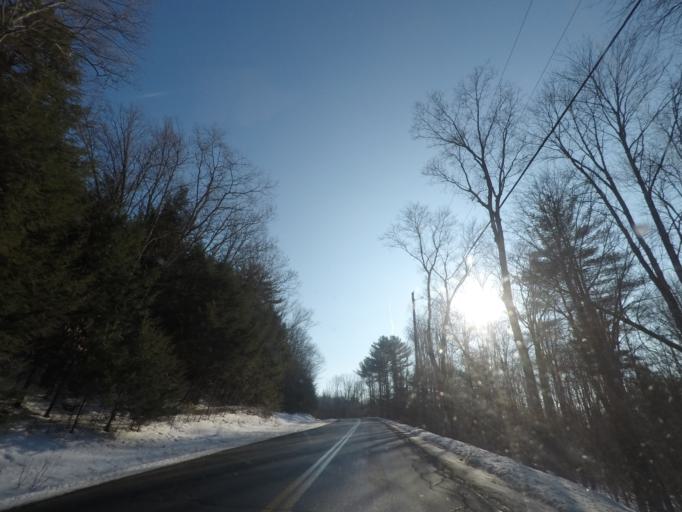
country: US
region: Massachusetts
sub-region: Berkshire County
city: Richmond
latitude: 42.5203
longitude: -73.4154
